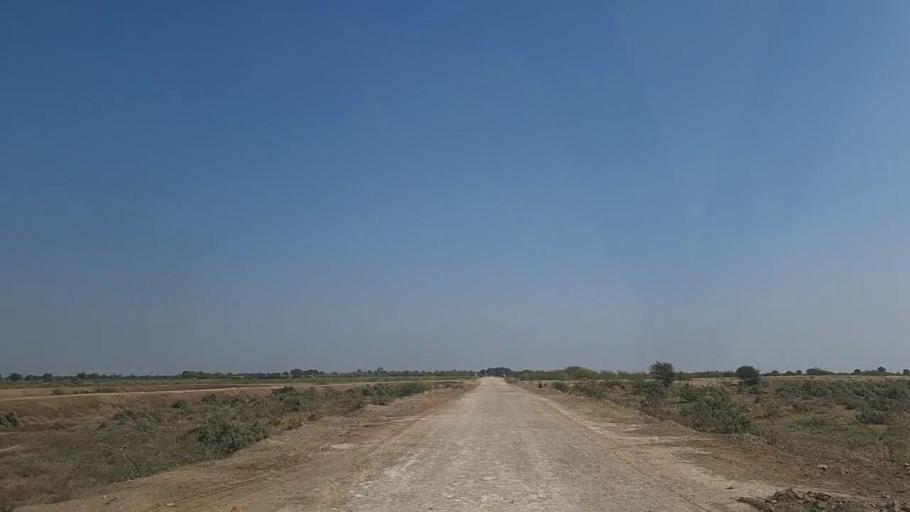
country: PK
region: Sindh
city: Digri
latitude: 25.1615
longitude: 69.1814
